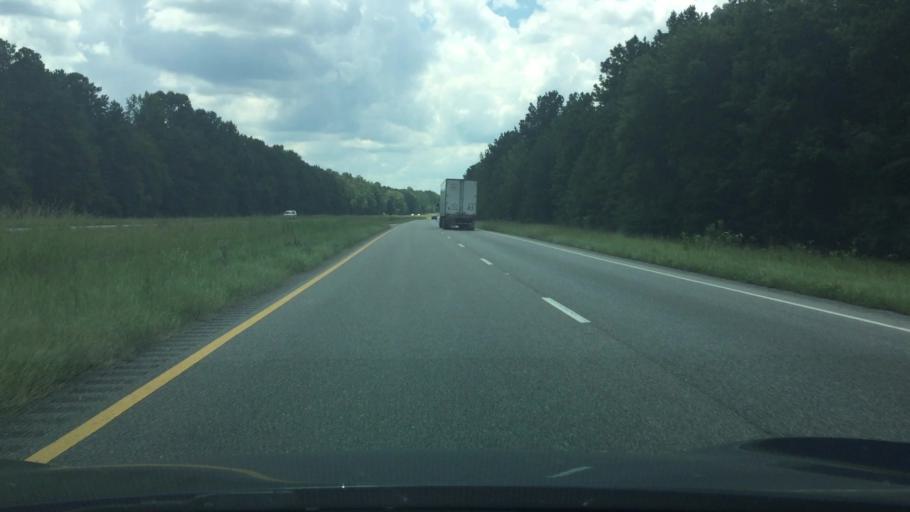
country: US
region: Alabama
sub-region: Pike County
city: Troy
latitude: 31.9980
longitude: -86.0275
